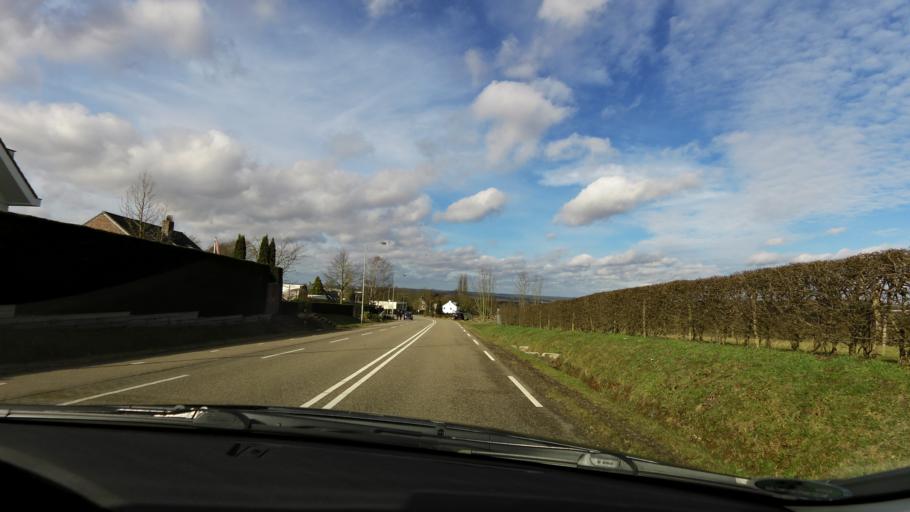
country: NL
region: Limburg
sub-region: Gemeente Meerssen
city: Meerssen
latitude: 50.8863
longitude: 5.7672
